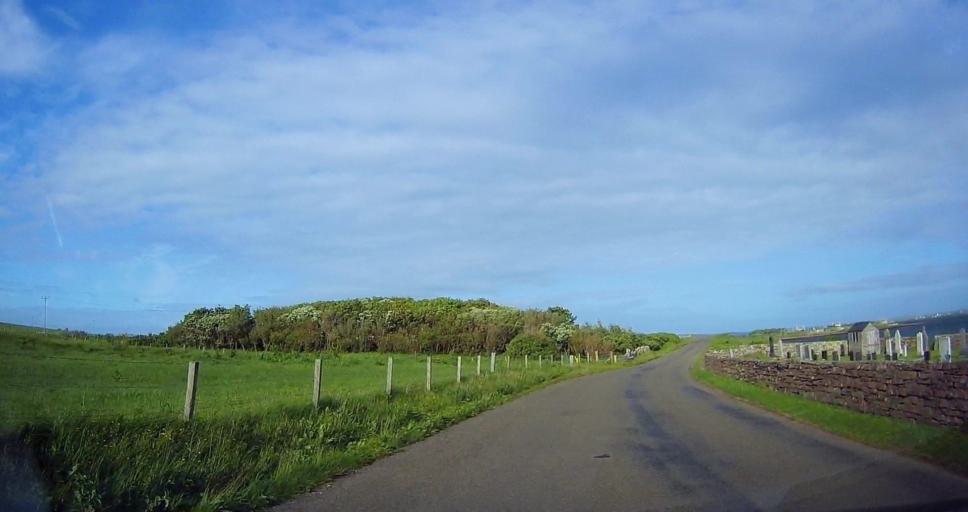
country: GB
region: Scotland
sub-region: Orkney Islands
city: Stromness
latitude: 58.8059
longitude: -3.2181
